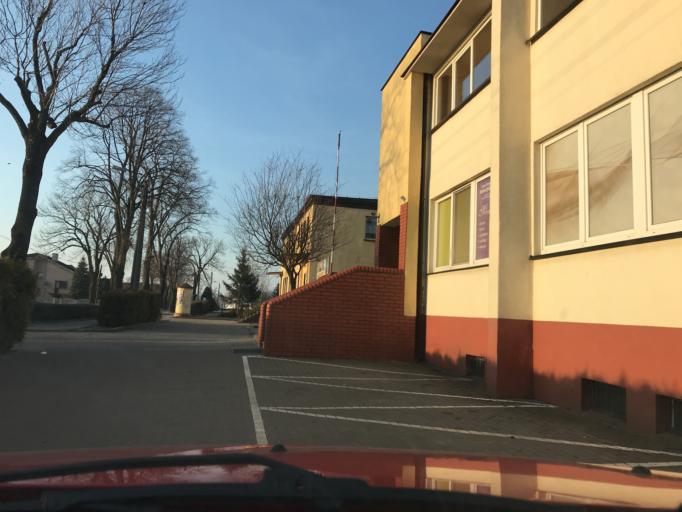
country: PL
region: Greater Poland Voivodeship
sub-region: Powiat jarocinski
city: Kotlin
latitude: 51.9165
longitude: 17.6528
